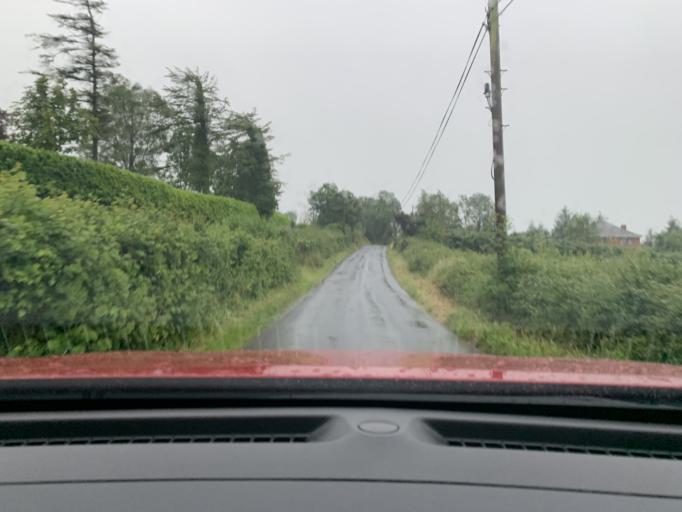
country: IE
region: Connaught
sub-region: Sligo
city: Sligo
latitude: 54.3347
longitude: -8.4113
